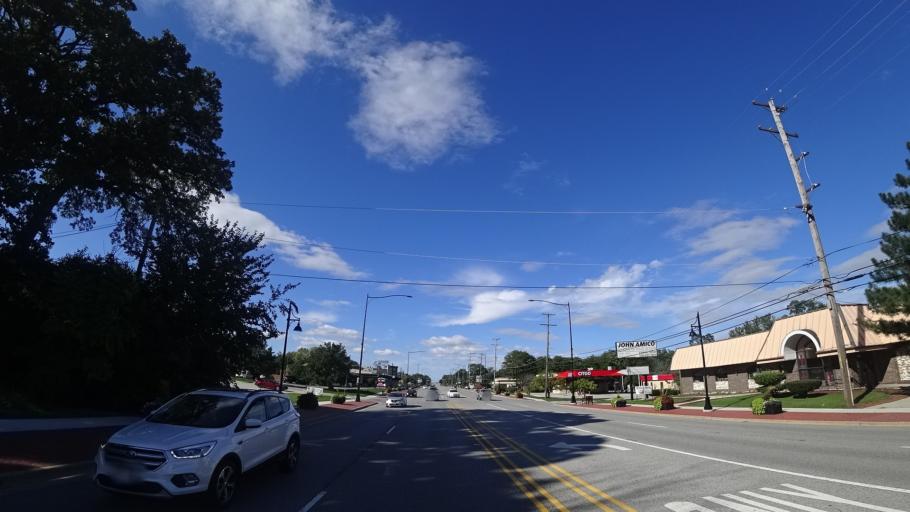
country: US
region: Illinois
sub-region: Cook County
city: Oak Forest
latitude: 41.6137
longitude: -87.7371
